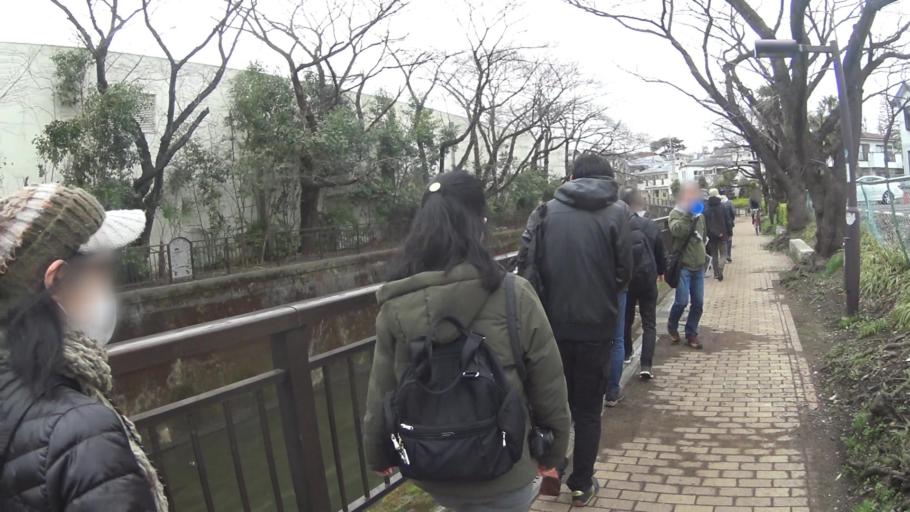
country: JP
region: Tokyo
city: Chofugaoka
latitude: 35.6372
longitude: 139.6043
